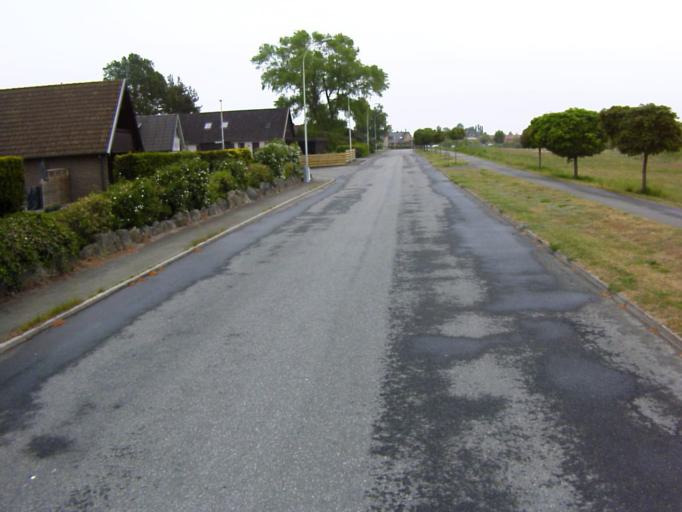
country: SE
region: Skane
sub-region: Kristianstads Kommun
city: Ahus
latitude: 55.9277
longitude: 14.2864
